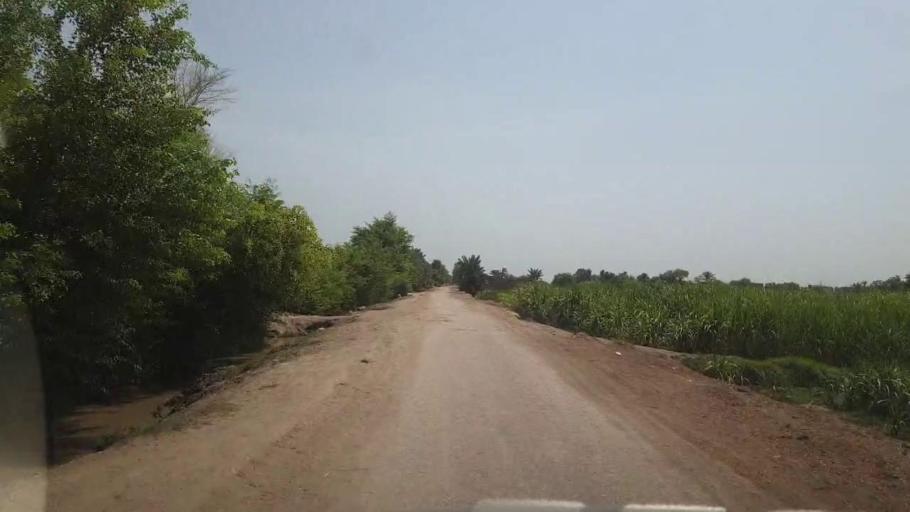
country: PK
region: Sindh
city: Sobhadero
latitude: 27.4410
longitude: 68.4028
